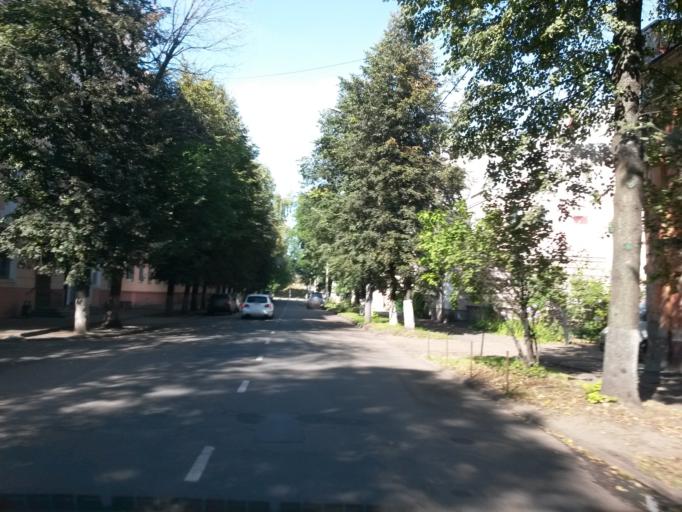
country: RU
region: Jaroslavl
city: Yaroslavl
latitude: 57.6373
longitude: 39.8879
